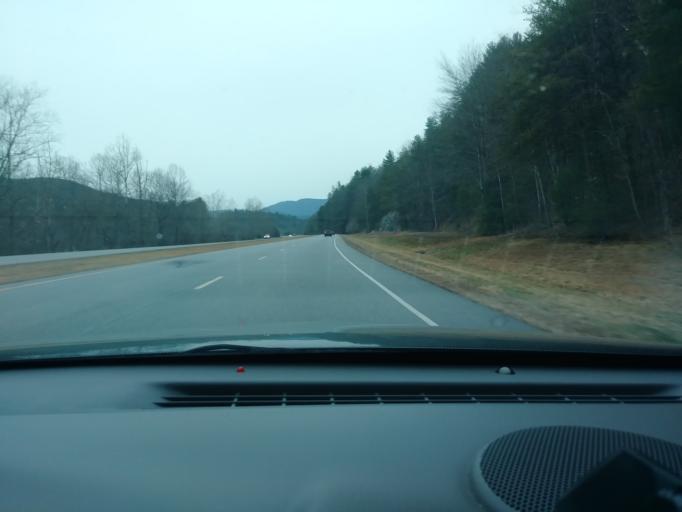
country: US
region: North Carolina
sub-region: Wilkes County
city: Millers Creek
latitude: 36.1824
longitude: -81.3986
